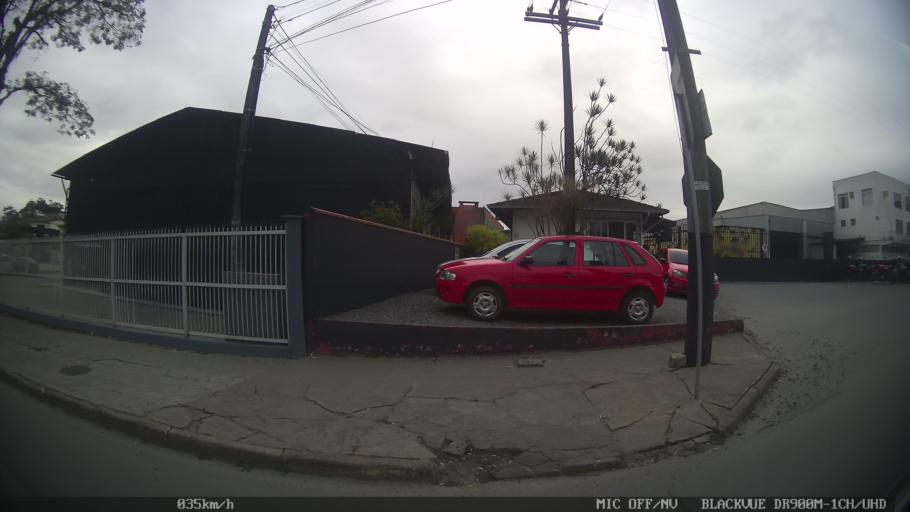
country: BR
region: Santa Catarina
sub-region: Joinville
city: Joinville
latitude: -26.2845
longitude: -48.8825
